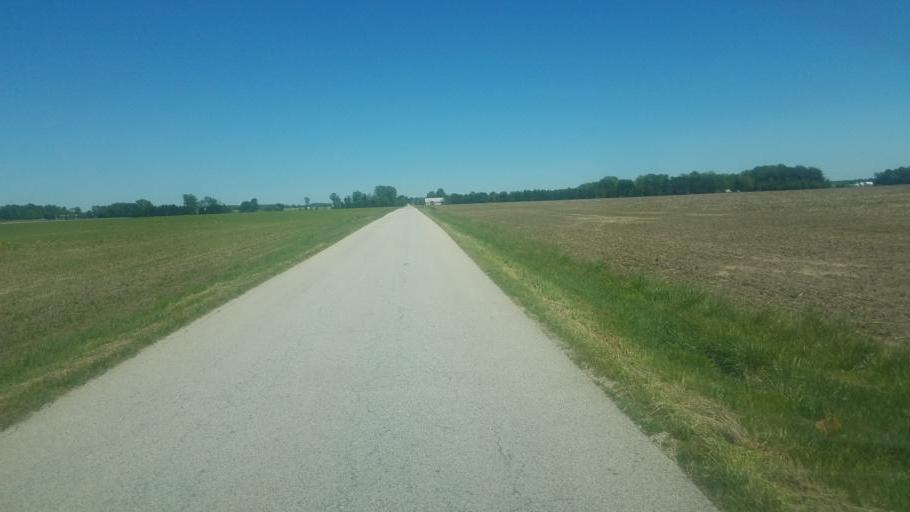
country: US
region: Ohio
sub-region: Shelby County
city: Sidney
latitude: 40.2005
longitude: -84.0688
